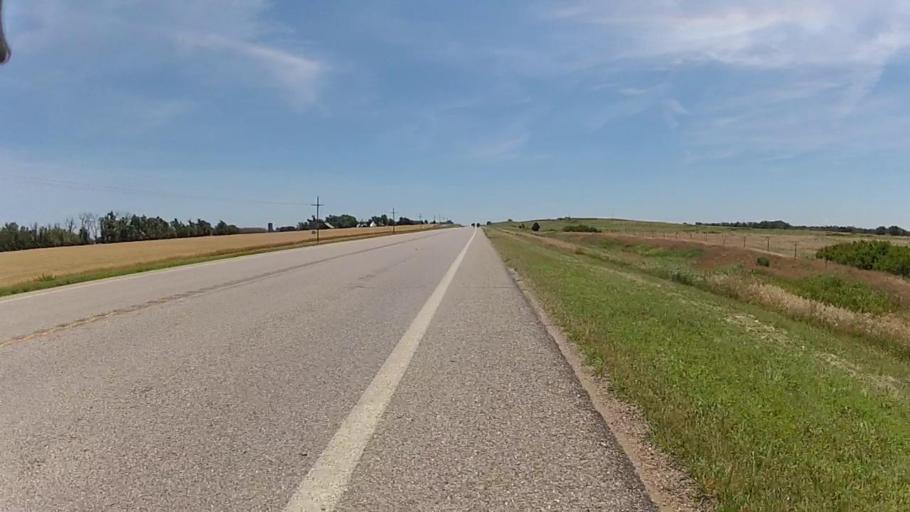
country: US
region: Kansas
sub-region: Barber County
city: Medicine Lodge
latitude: 37.2537
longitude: -98.4834
